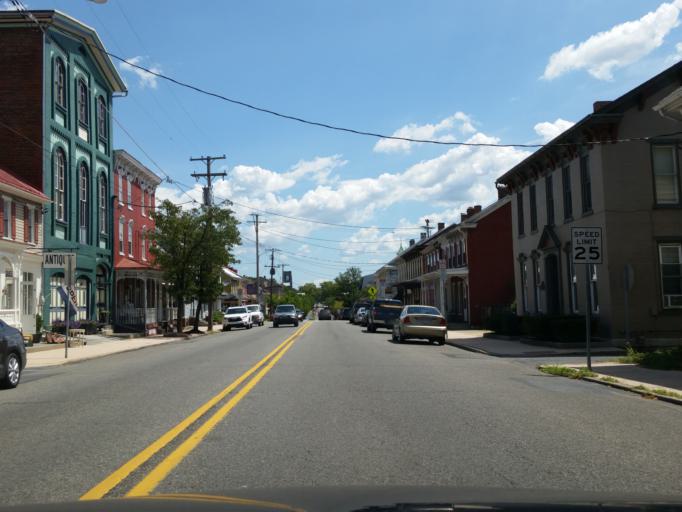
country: US
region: Pennsylvania
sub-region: Lebanon County
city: Annville
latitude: 40.3285
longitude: -76.5198
